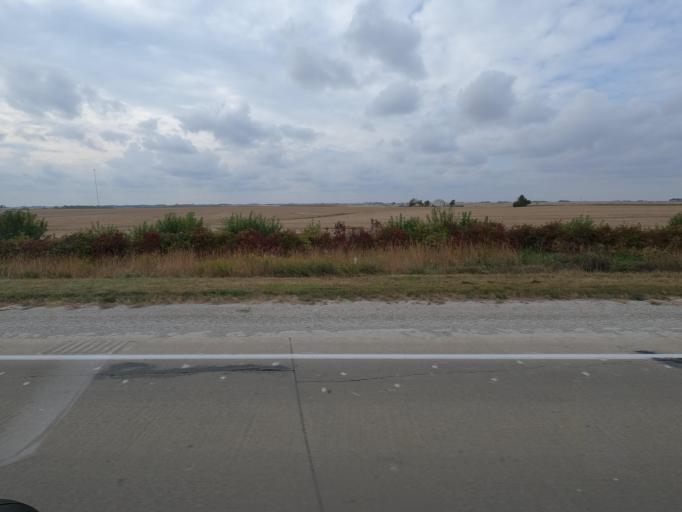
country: US
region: Iowa
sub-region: Jasper County
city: Monroe
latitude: 41.5352
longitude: -93.1304
